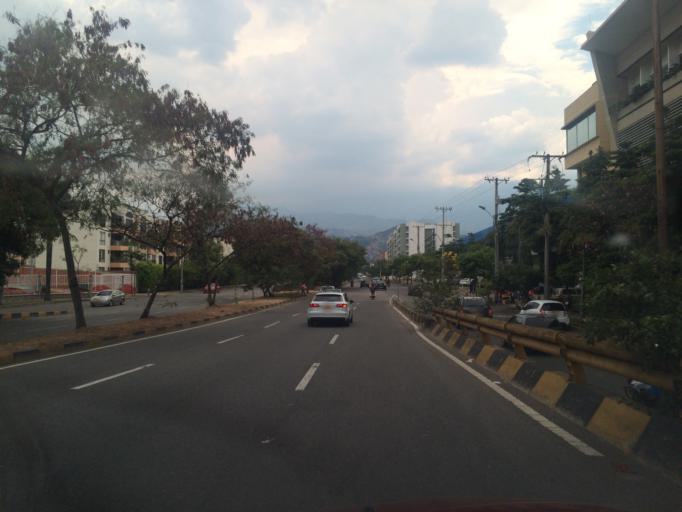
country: CO
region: Valle del Cauca
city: Cali
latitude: 3.3868
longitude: -76.5396
